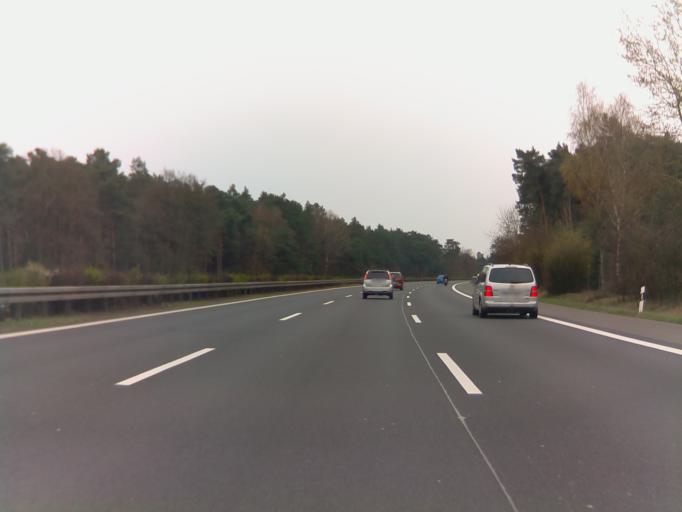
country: DE
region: Brandenburg
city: Fichtenwalde
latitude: 52.2413
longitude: 12.9167
